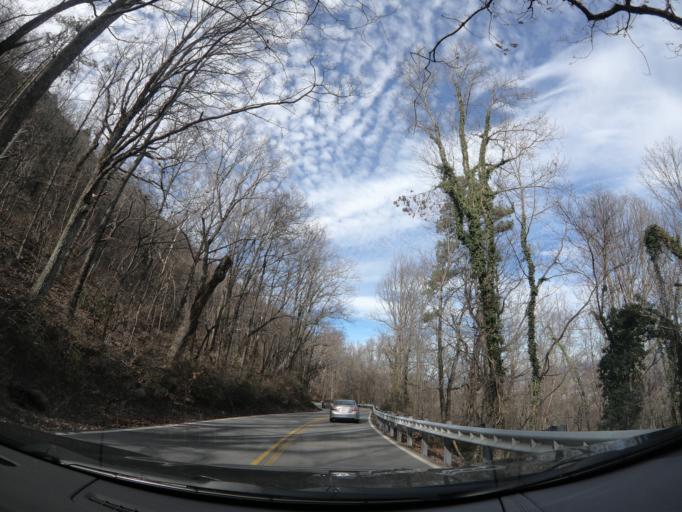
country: US
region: Tennessee
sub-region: Hamilton County
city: Lookout Mountain
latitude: 34.9979
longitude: -85.3419
